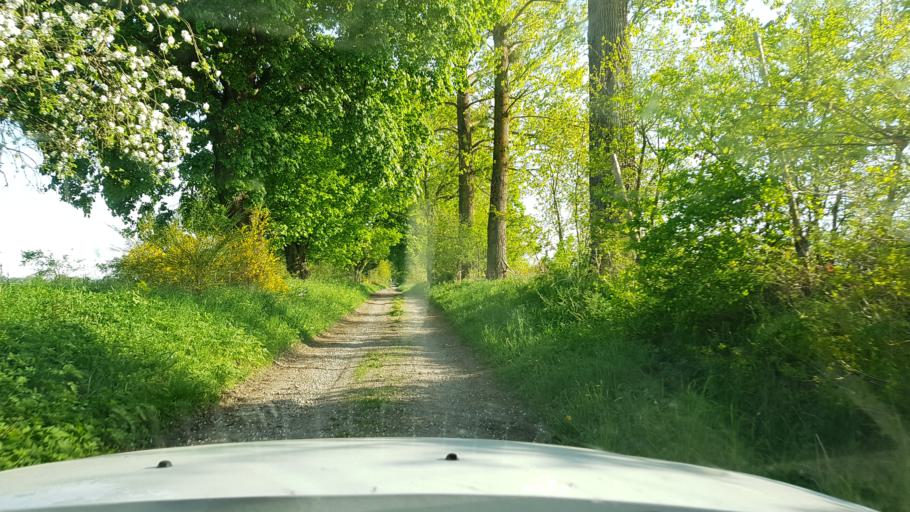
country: PL
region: West Pomeranian Voivodeship
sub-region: Powiat lobeski
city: Resko
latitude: 53.6962
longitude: 15.3360
